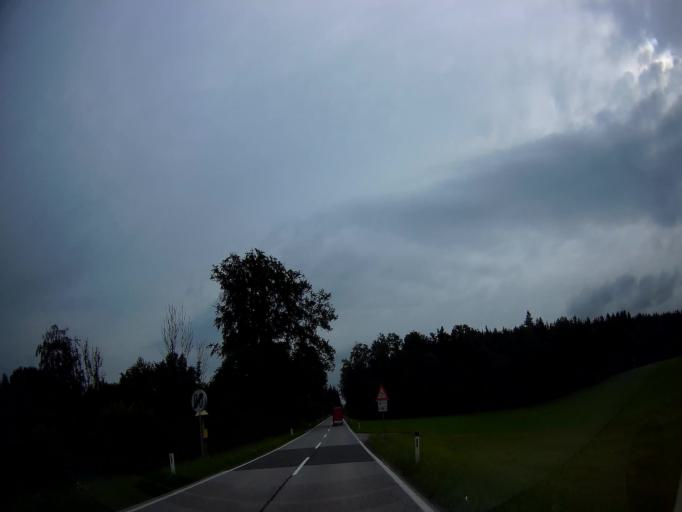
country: AT
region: Salzburg
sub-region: Politischer Bezirk Salzburg-Umgebung
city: Mattsee
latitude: 48.0331
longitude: 13.1435
